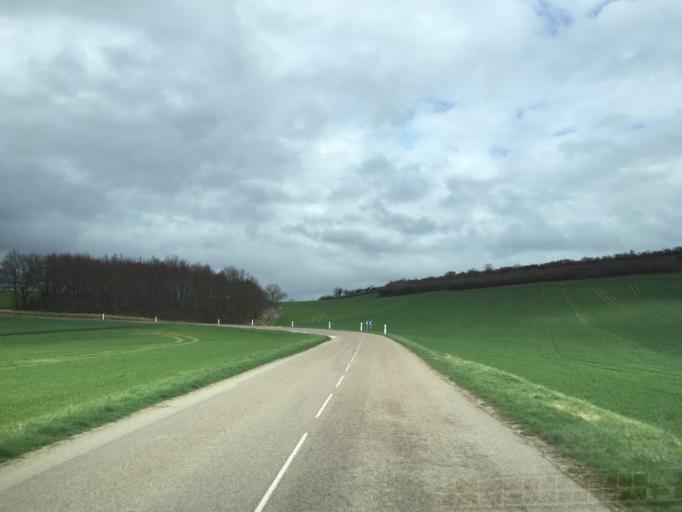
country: FR
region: Bourgogne
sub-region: Departement de l'Yonne
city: Pourrain
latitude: 47.7924
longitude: 3.4071
